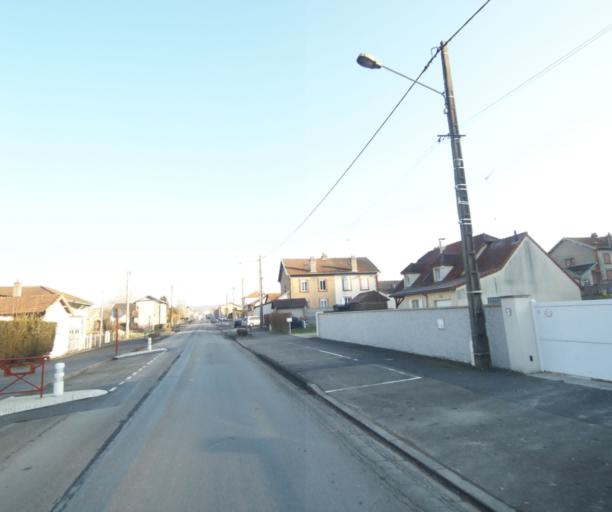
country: FR
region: Champagne-Ardenne
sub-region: Departement de la Haute-Marne
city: Bienville
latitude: 48.5460
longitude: 5.0822
